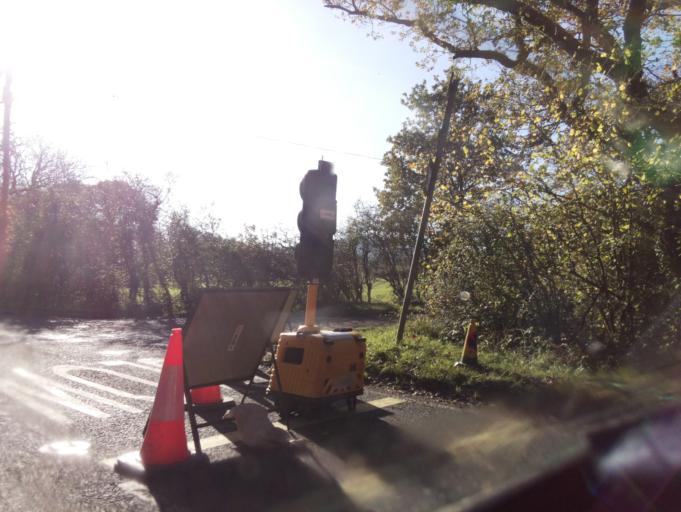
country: GB
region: England
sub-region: Dorset
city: Sherborne
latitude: 50.8610
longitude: -2.4673
